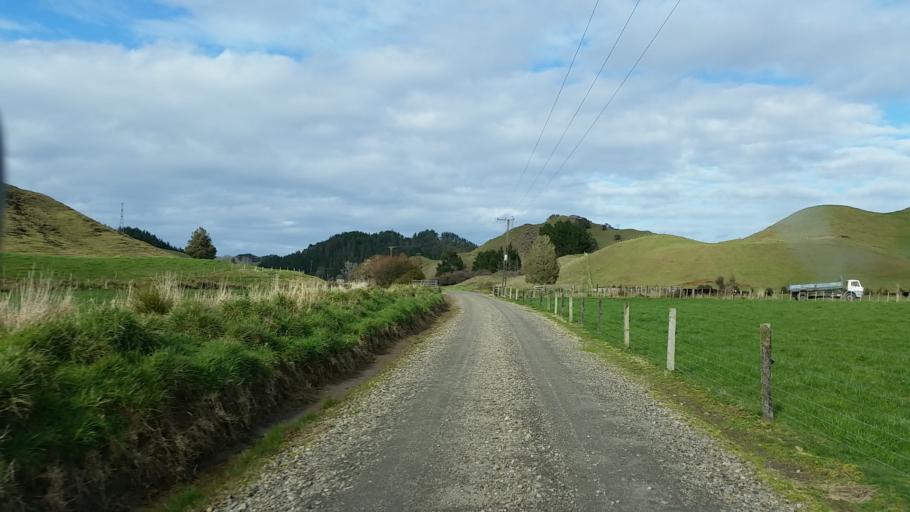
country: NZ
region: Taranaki
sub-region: South Taranaki District
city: Eltham
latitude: -39.2245
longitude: 174.5630
